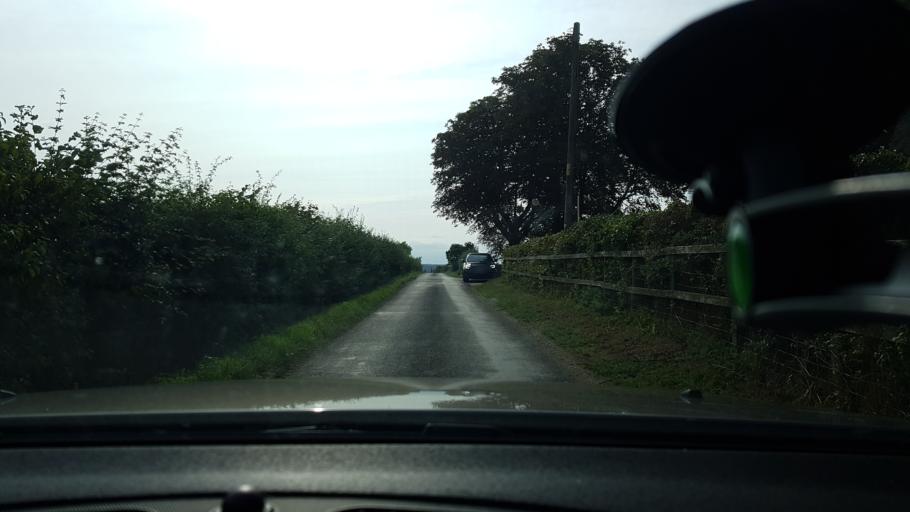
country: GB
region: England
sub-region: Wiltshire
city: Ramsbury
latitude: 51.4495
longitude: -1.5745
